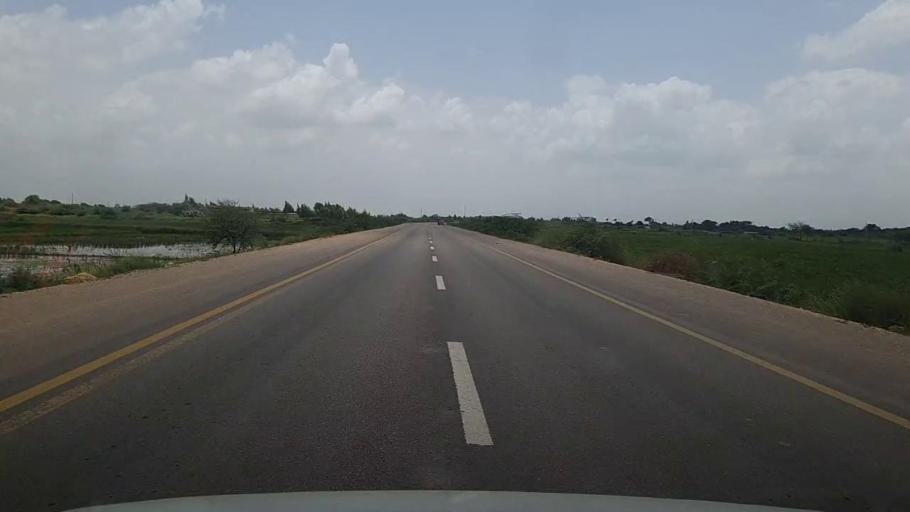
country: PK
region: Sindh
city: Thatta
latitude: 24.7546
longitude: 67.9527
